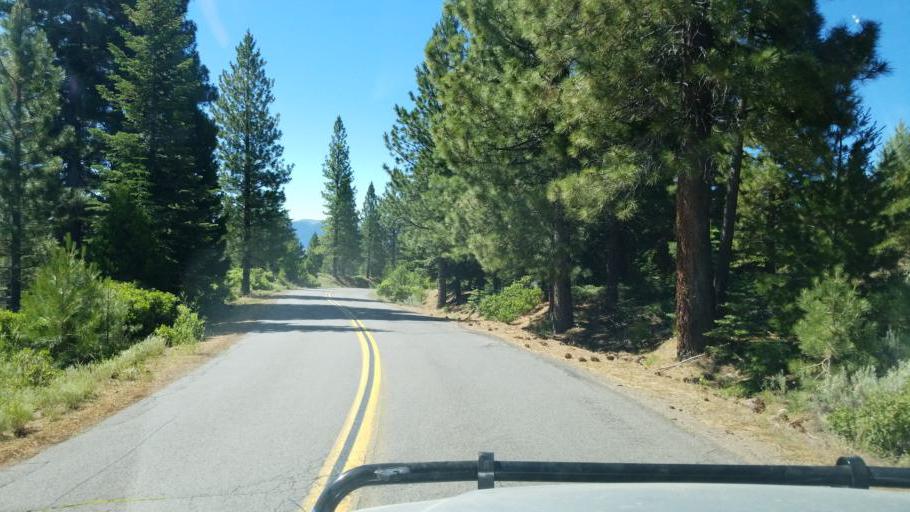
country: US
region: California
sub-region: Lassen County
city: Susanville
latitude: 40.4712
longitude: -120.7564
